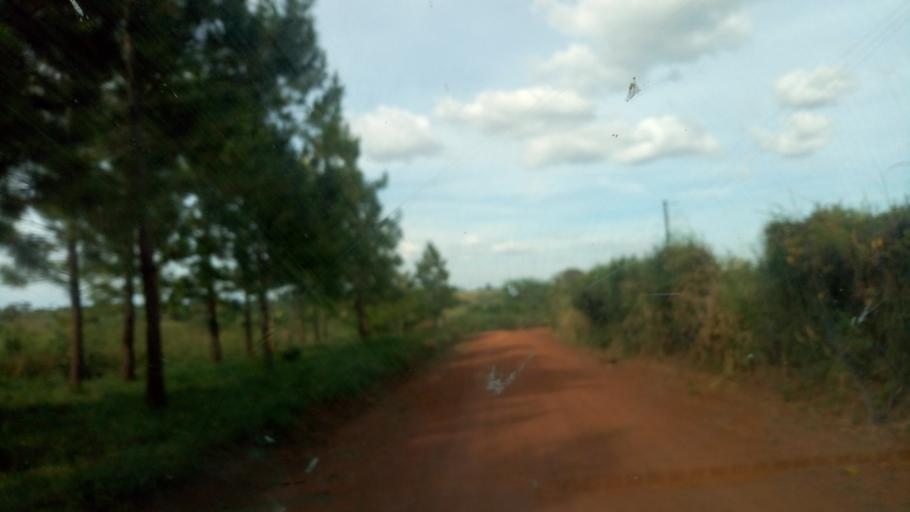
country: UG
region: Western Region
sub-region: Kiryandongo District
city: Kiryandongo
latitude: 1.8164
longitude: 31.9333
